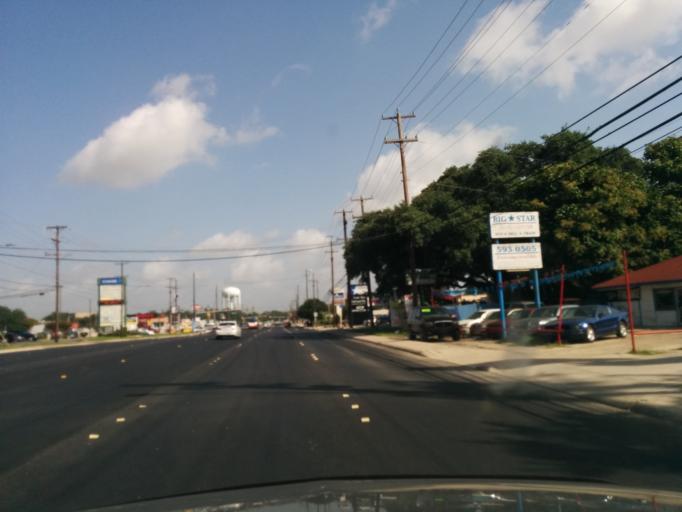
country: US
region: Texas
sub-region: Bexar County
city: Balcones Heights
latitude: 29.5113
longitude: -98.5675
